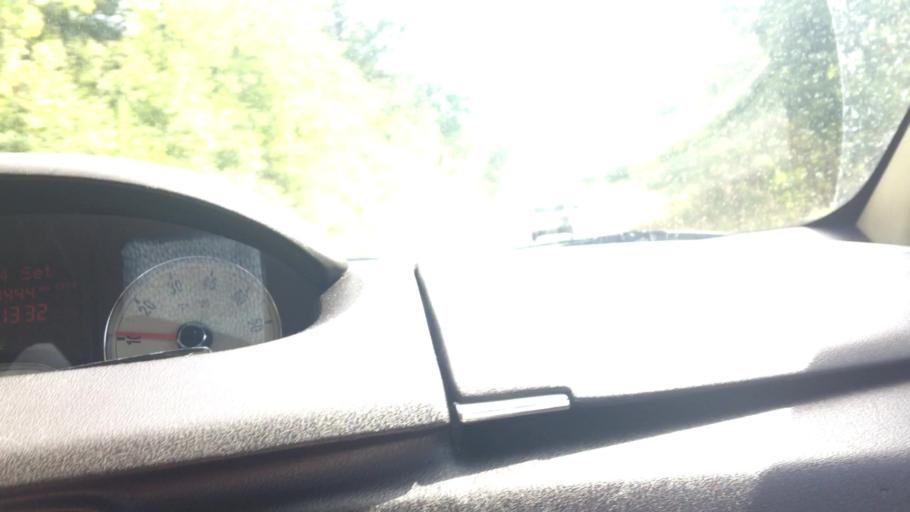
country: IT
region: Molise
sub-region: Provincia di Isernia
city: Carovilli
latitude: 41.7317
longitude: 14.2676
